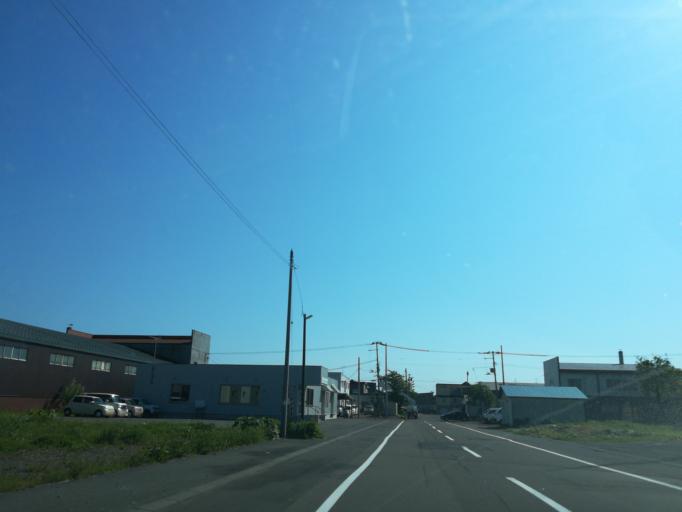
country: JP
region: Hokkaido
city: Iwamizawa
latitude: 43.1888
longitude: 141.7447
